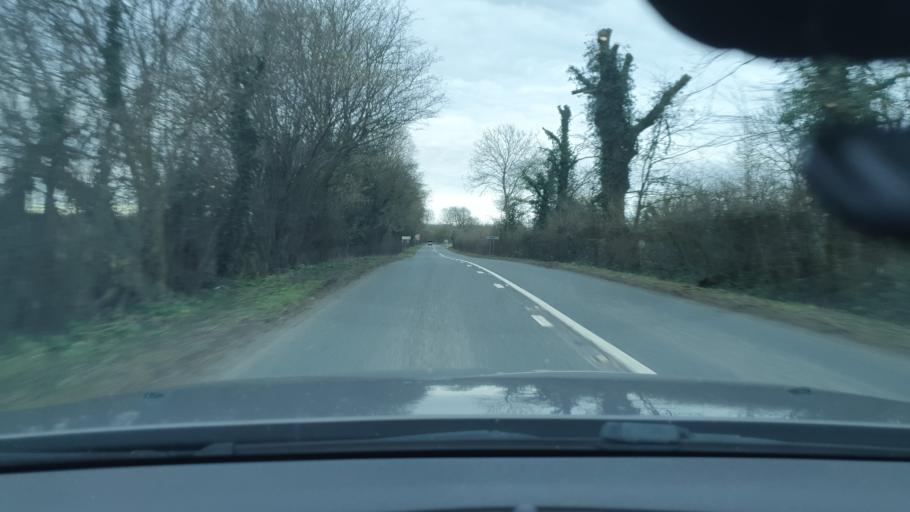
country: GB
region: England
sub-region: Wiltshire
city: Seend
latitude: 51.3363
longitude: -2.1148
